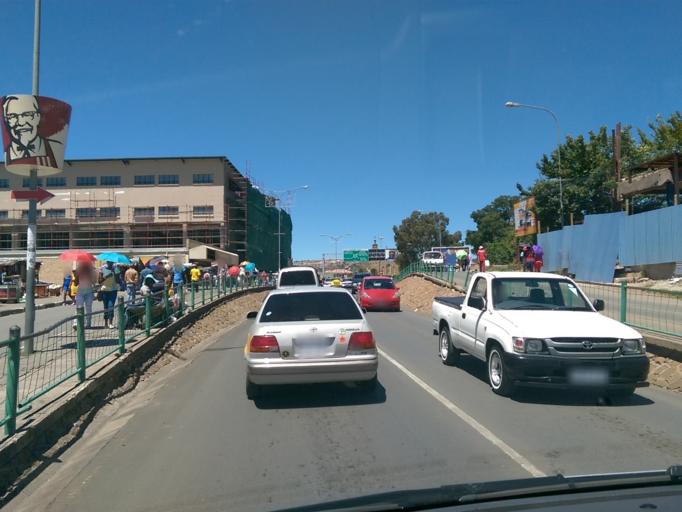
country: LS
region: Maseru
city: Maseru
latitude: -29.3157
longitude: 27.4916
